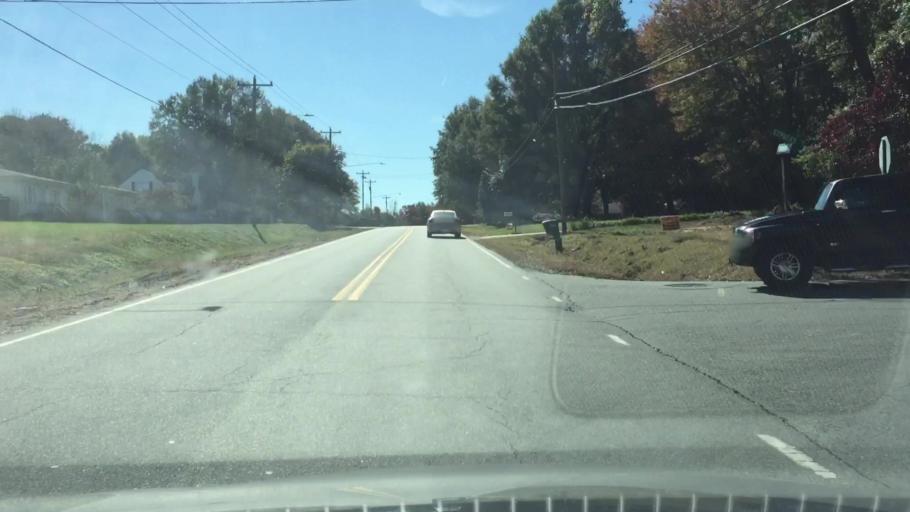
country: US
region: North Carolina
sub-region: Rockingham County
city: Reidsville
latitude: 36.3265
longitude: -79.6661
